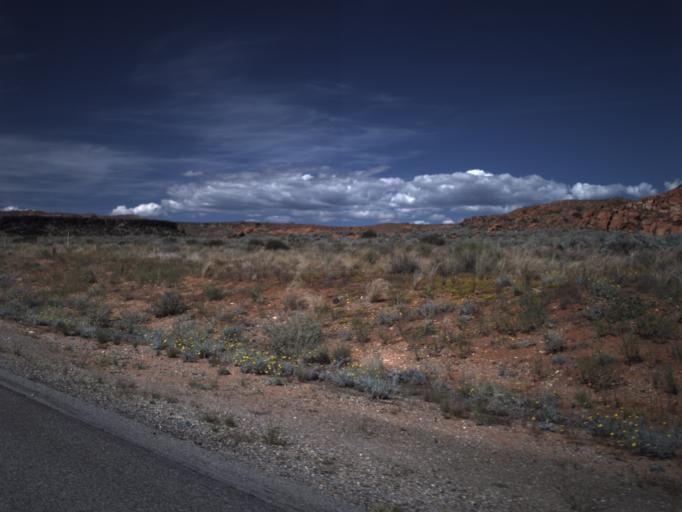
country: US
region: Utah
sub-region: Washington County
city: Santa Clara
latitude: 37.1598
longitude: -113.6050
